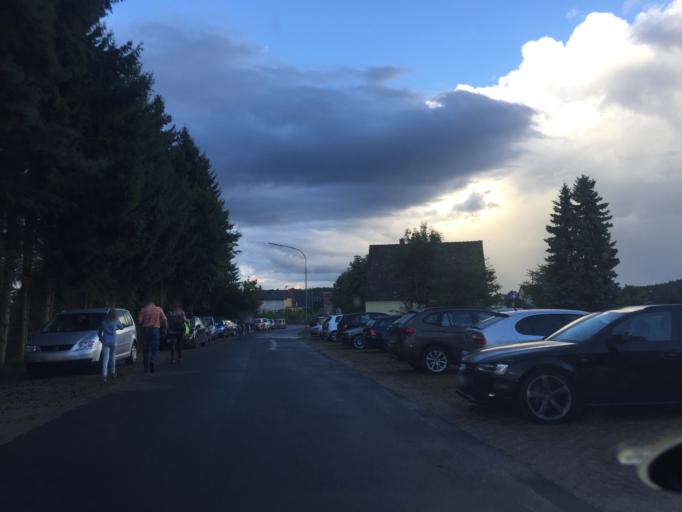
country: DE
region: Bavaria
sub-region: Upper Palatinate
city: Pressath
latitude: 49.7599
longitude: 11.9438
